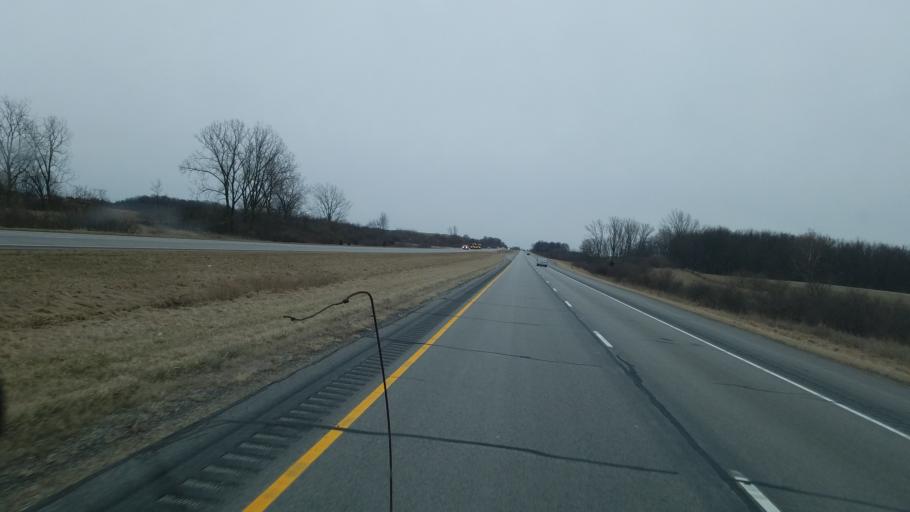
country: US
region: Indiana
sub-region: Marshall County
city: Argos
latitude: 41.1912
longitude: -86.2517
